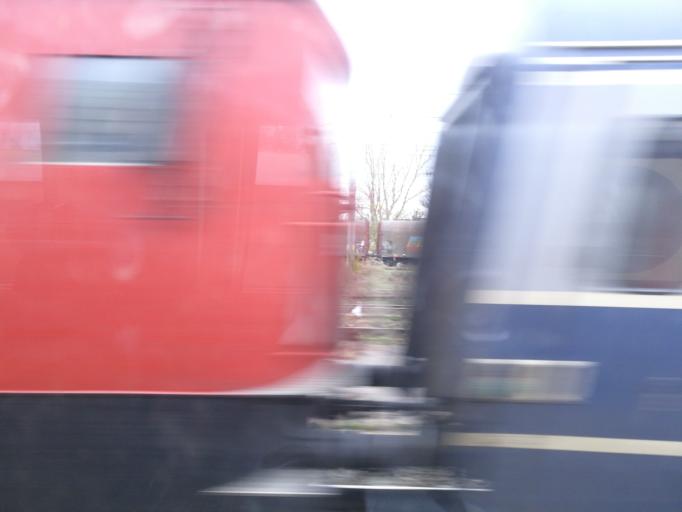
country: RO
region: Bacau
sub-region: Municipiul Bacau
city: Bacau
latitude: 46.5648
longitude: 26.8957
